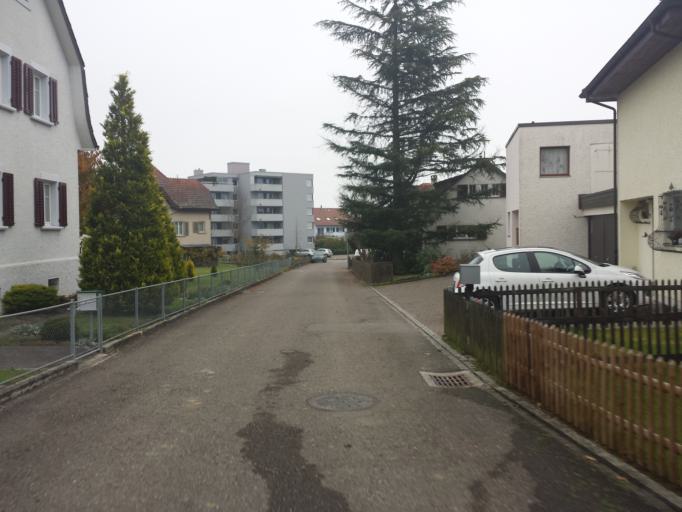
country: CH
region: Thurgau
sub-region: Arbon District
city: Salmsach
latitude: 47.5649
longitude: 9.3590
